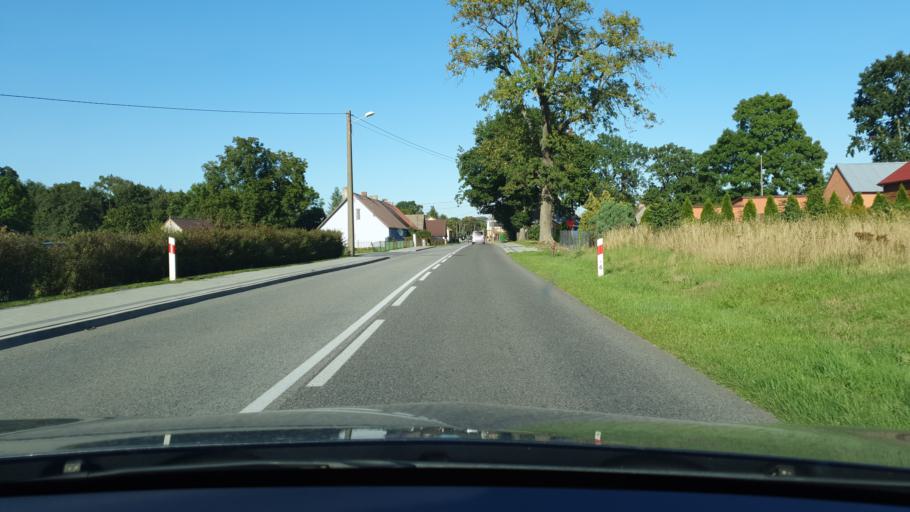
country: PL
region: West Pomeranian Voivodeship
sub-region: Powiat kamienski
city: Golczewo
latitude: 53.8306
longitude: 14.8764
